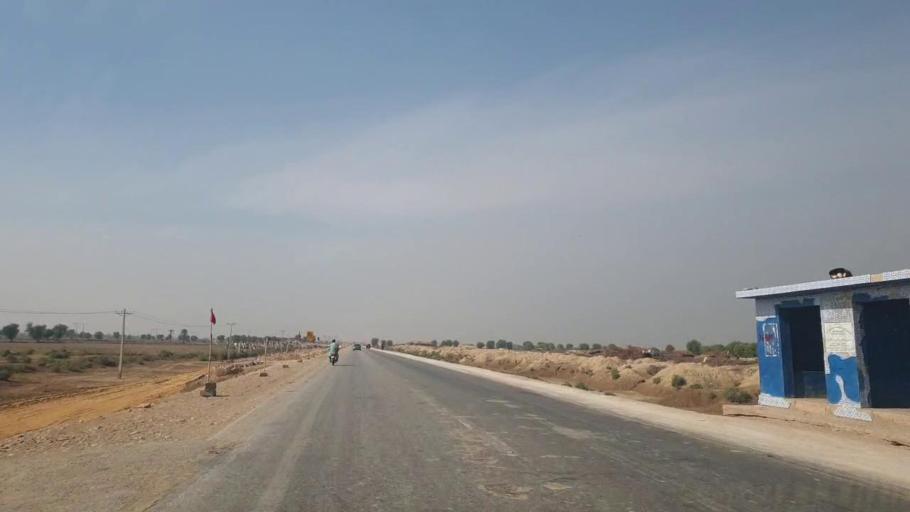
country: PK
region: Sindh
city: Sann
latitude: 25.9994
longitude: 68.1637
